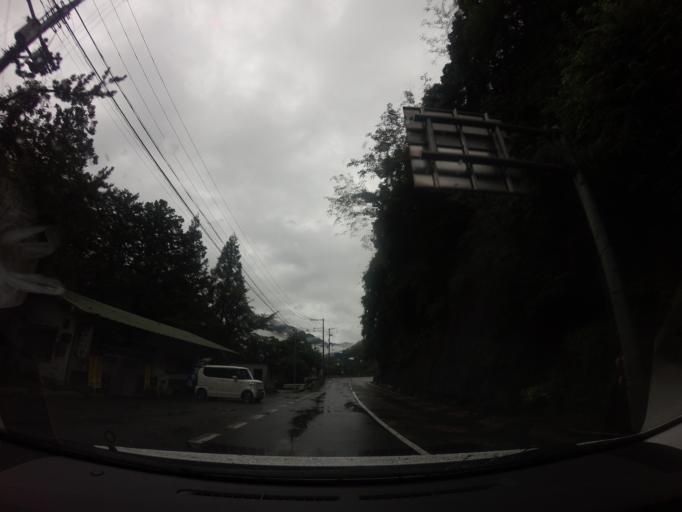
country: JP
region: Wakayama
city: Koya
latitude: 34.0608
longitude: 135.7447
